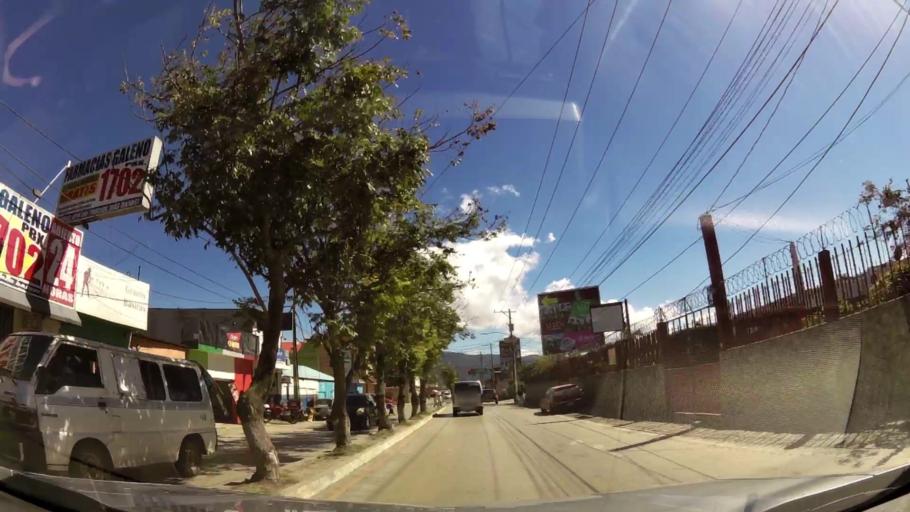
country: GT
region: Guatemala
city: San Jose Pinula
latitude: 14.5460
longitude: -90.4102
